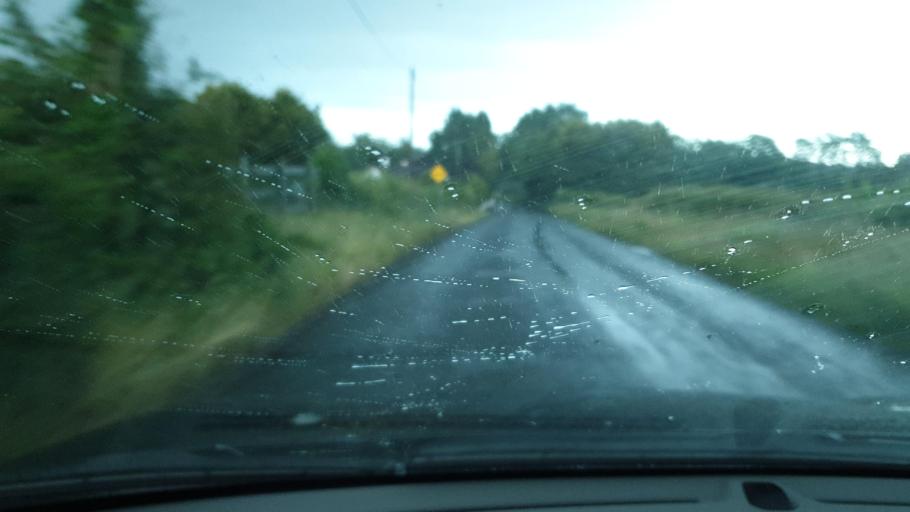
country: IE
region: Leinster
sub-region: An Mhi
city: Navan
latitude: 53.6302
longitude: -6.6687
